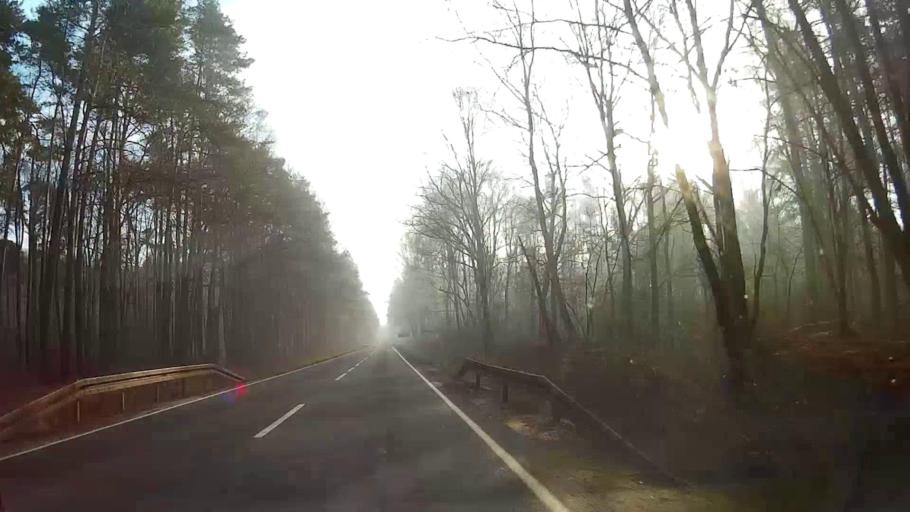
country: PL
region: Lesser Poland Voivodeship
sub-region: Powiat chrzanowski
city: Metkow
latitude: 50.0760
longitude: 19.3852
